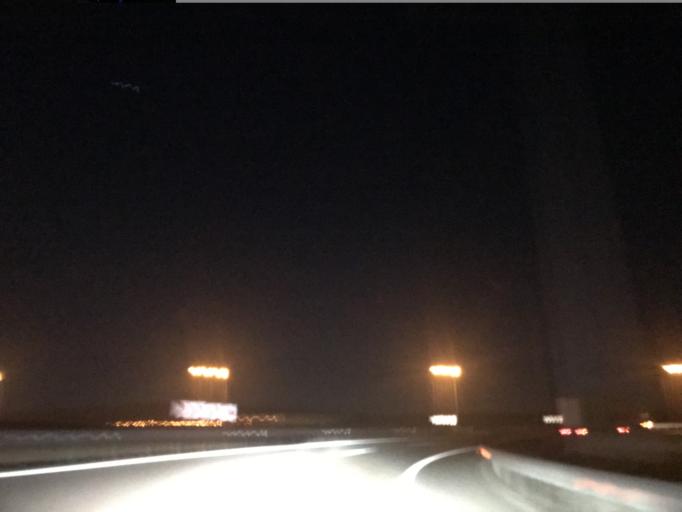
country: TR
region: Nigde
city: Ulukisla
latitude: 37.6430
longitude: 34.3586
